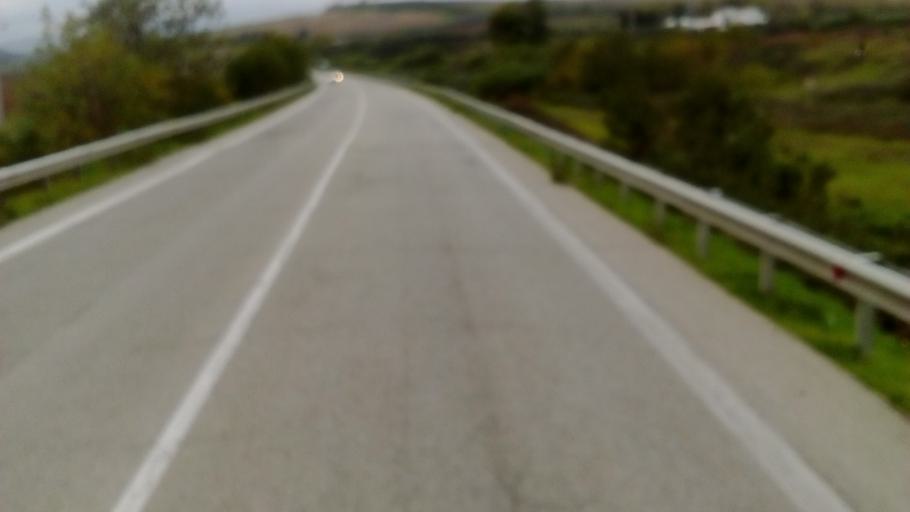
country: IT
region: Abruzzo
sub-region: Provincia di Chieti
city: San Salvo
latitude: 42.0252
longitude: 14.7354
